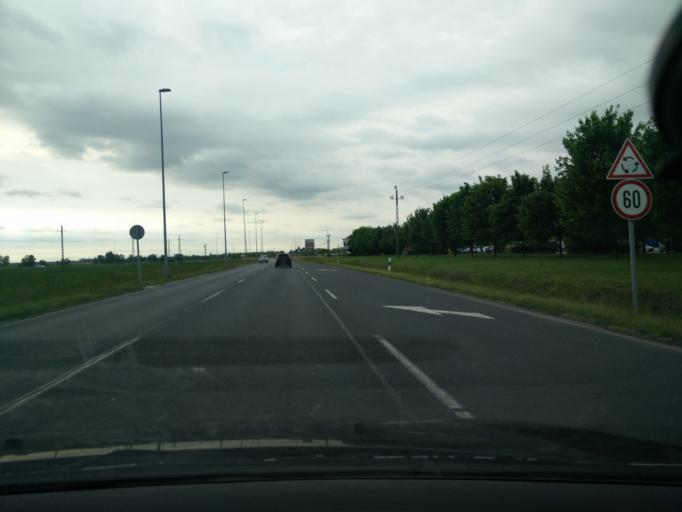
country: HU
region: Veszprem
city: Papa
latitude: 47.3200
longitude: 17.4487
